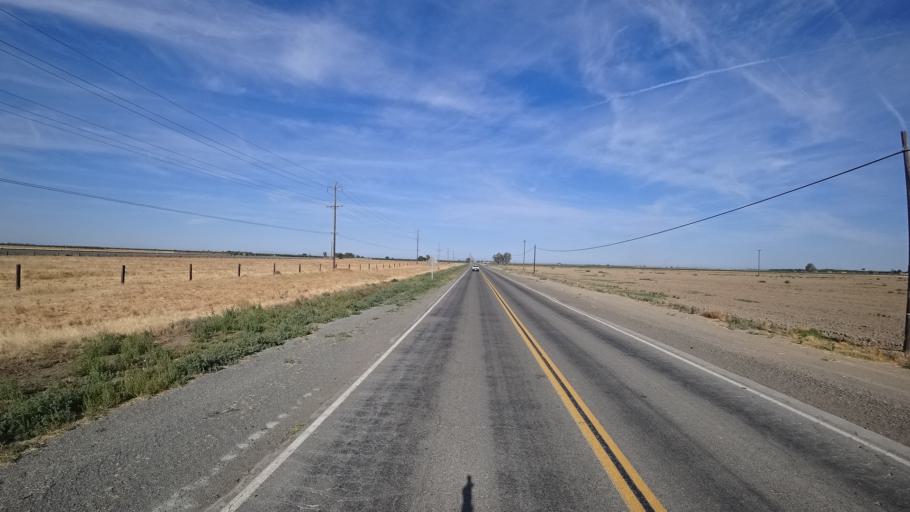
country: US
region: California
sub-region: Kings County
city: Home Garden
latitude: 36.3429
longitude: -119.5365
